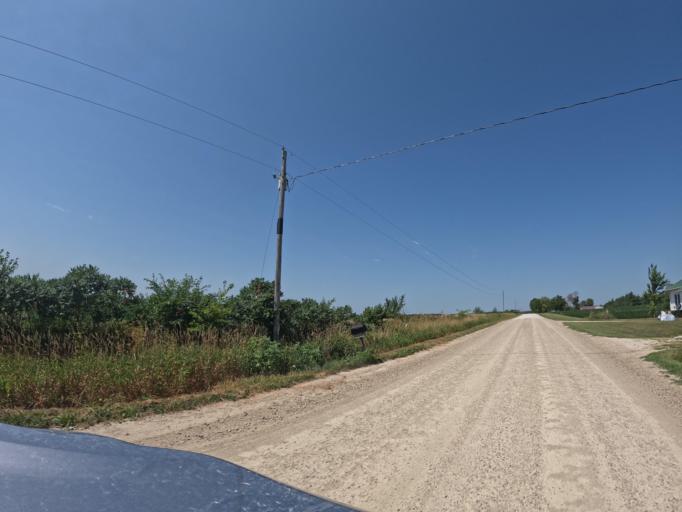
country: US
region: Iowa
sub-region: Henry County
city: Mount Pleasant
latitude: 40.8893
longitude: -91.5881
